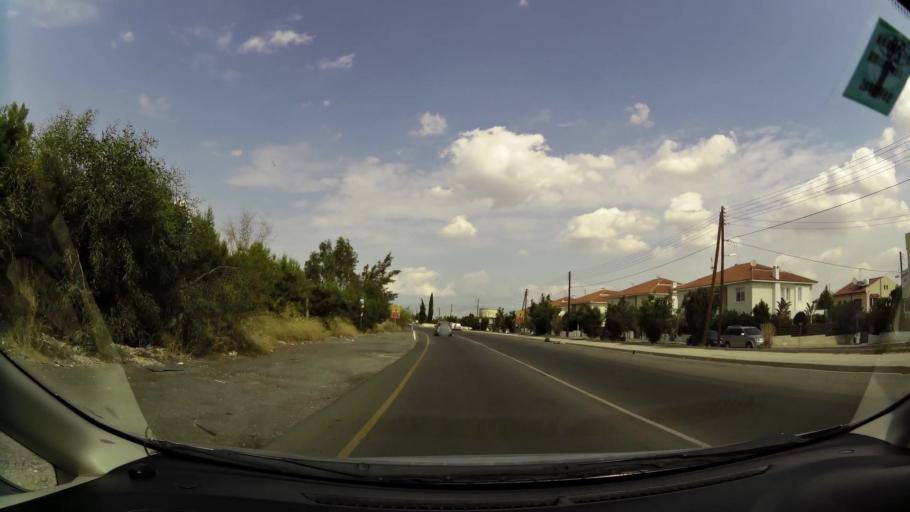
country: CY
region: Lefkosia
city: Tseri
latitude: 35.1095
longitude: 33.3318
